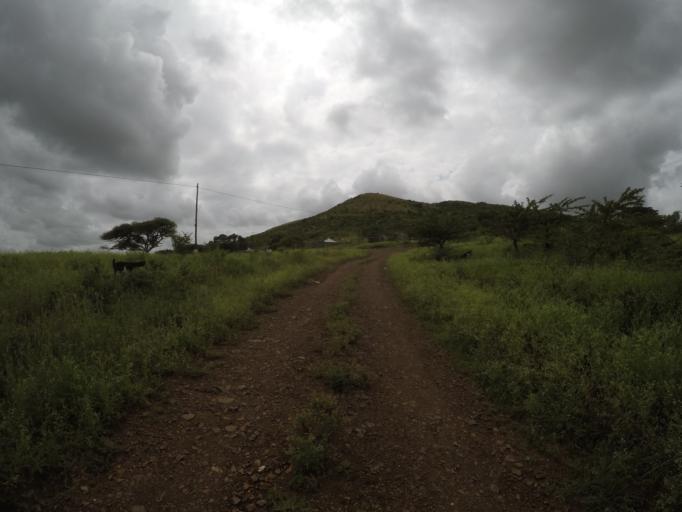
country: ZA
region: KwaZulu-Natal
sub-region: uThungulu District Municipality
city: Empangeni
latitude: -28.6075
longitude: 31.8941
